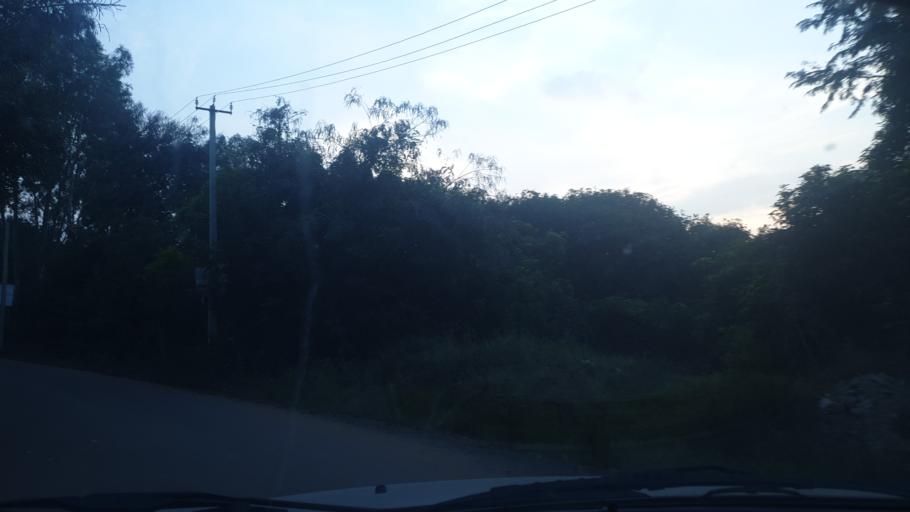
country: IN
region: Karnataka
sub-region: Bangalore Rural
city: Hoskote
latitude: 13.0880
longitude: 77.7012
